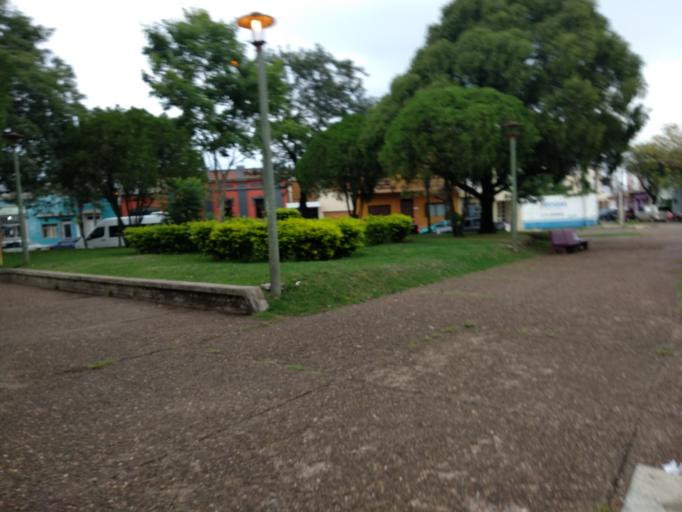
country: UY
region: Artigas
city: Artigas
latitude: -30.4038
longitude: -56.4697
